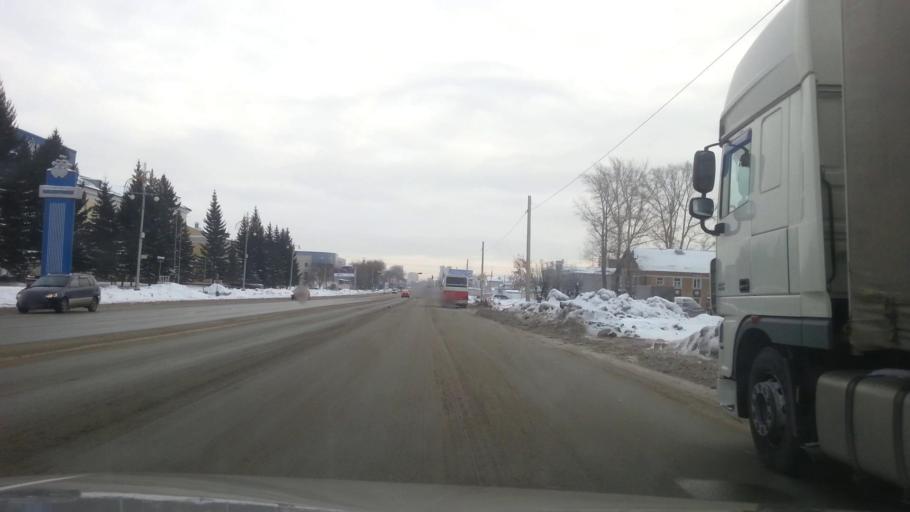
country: RU
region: Altai Krai
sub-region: Gorod Barnaulskiy
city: Barnaul
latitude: 53.3747
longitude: 83.7563
